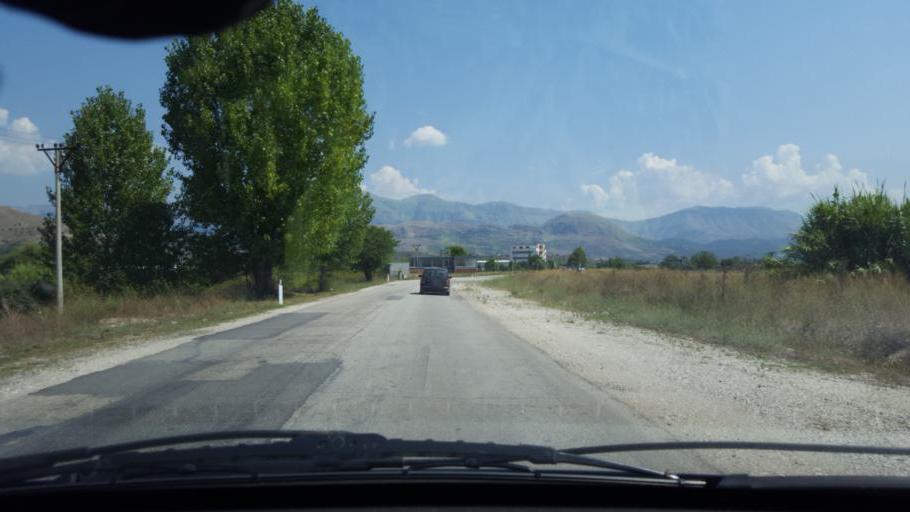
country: AL
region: Vlore
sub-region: Rrethi i Delvines
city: Finiq
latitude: 39.8878
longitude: 20.0598
